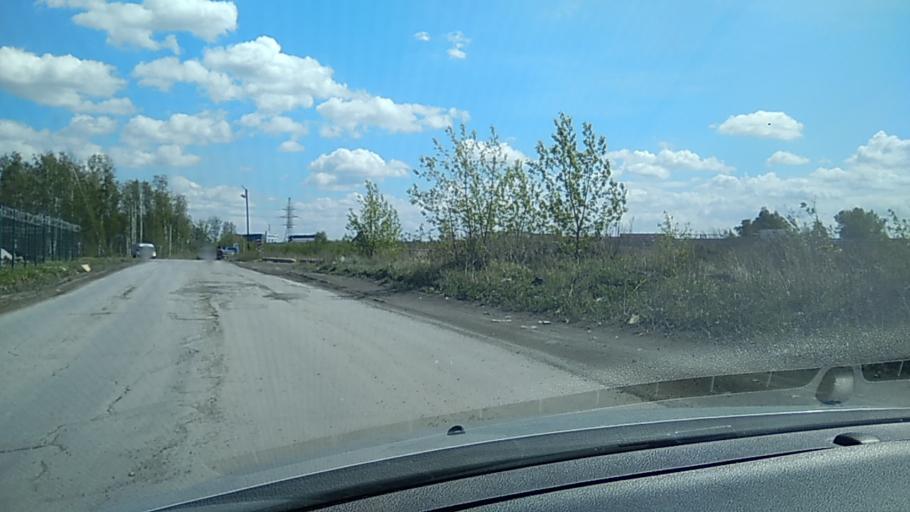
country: RU
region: Sverdlovsk
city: Istok
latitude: 56.7537
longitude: 60.7536
